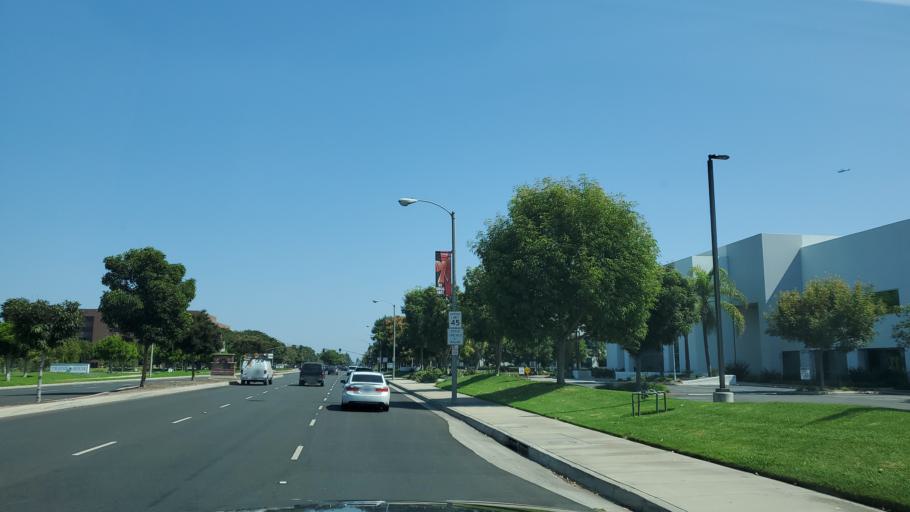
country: US
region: California
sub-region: Orange County
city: Cypress
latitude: 33.8029
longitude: -118.0368
